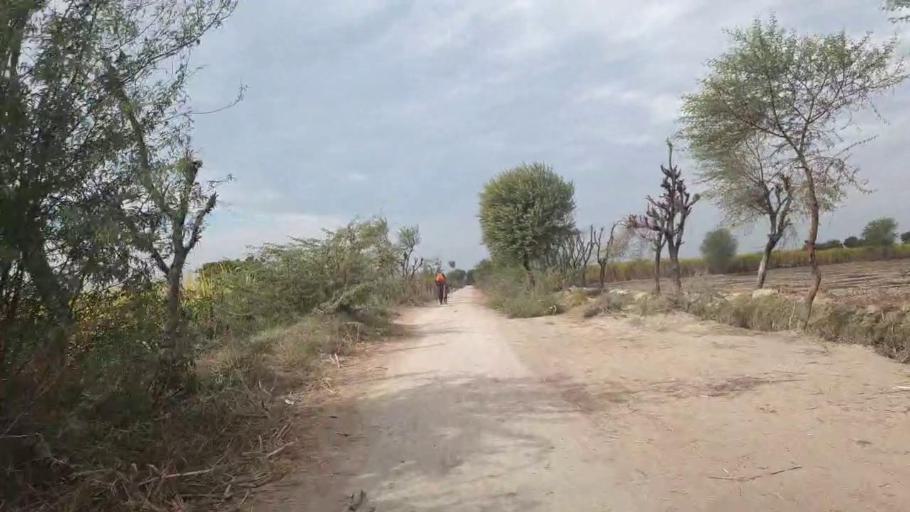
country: PK
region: Sindh
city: Jhol
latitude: 26.0062
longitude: 68.8738
